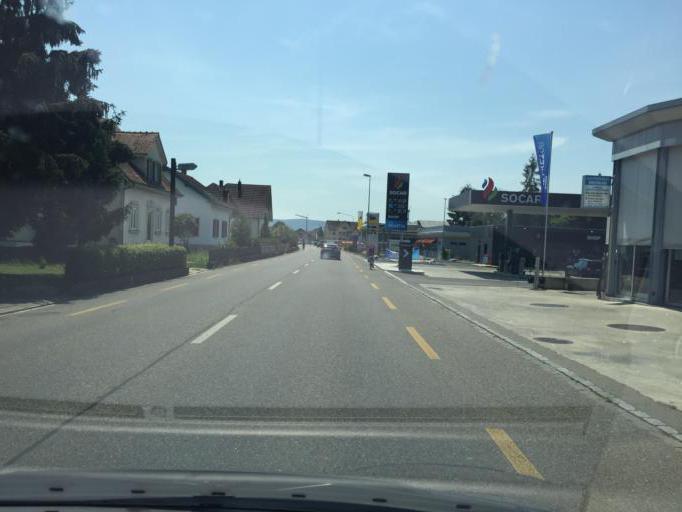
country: CH
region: Schaffhausen
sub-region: Bezirk Stein
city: Ramsen
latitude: 47.7103
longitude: 8.8214
